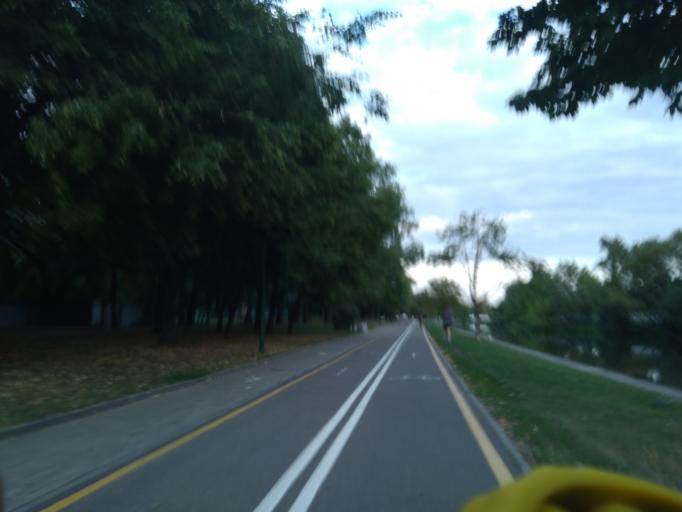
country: BY
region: Minsk
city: Minsk
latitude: 53.8973
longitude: 27.5774
